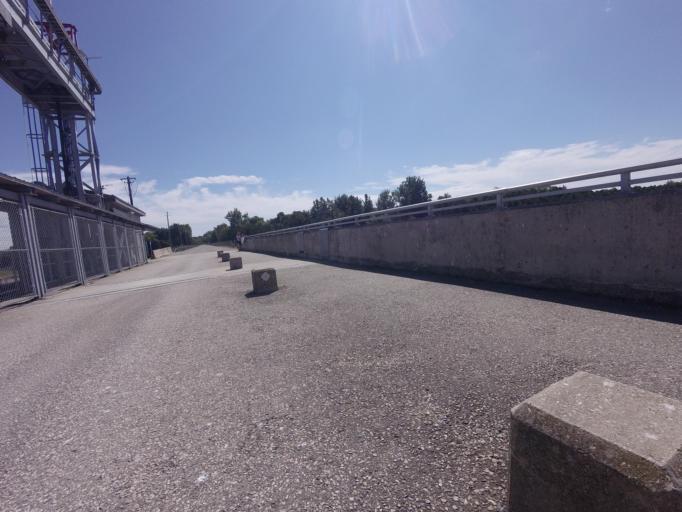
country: CA
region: Ontario
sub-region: Wellington County
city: Guelph
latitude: 43.7343
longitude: -80.3371
